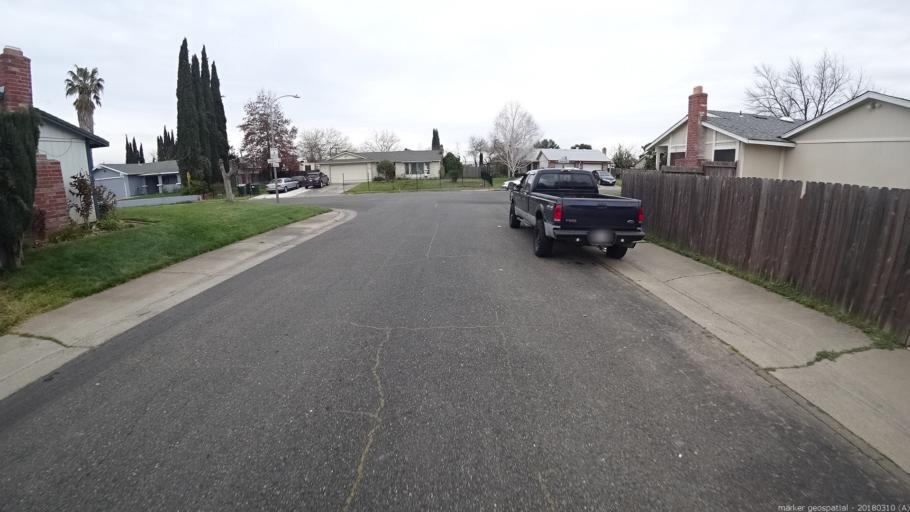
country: US
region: California
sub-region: Sacramento County
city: Florin
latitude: 38.4896
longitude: -121.3825
